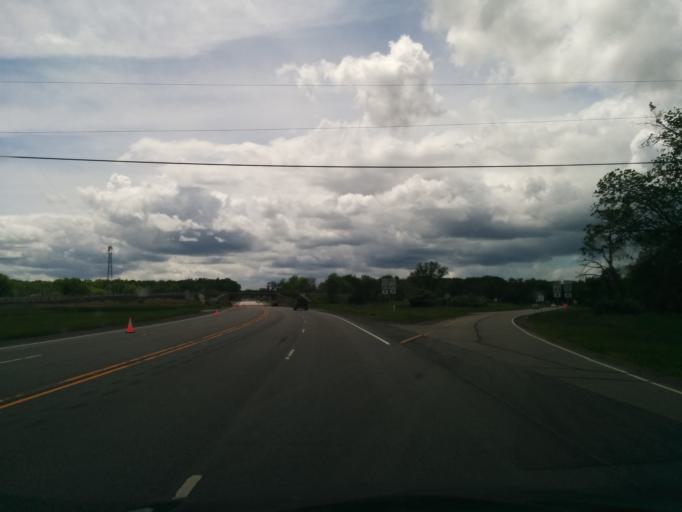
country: US
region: Indiana
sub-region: Porter County
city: Chesterton
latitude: 41.6367
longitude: -87.0549
